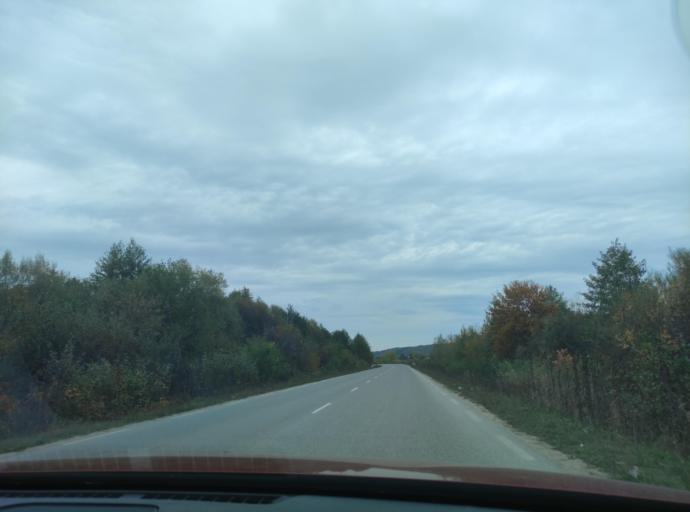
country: BG
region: Montana
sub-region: Obshtina Berkovitsa
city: Berkovitsa
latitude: 43.2375
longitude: 23.1610
